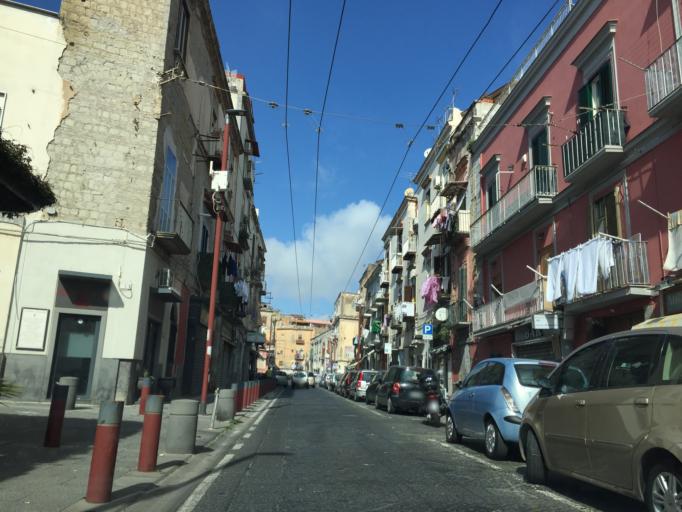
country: IT
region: Campania
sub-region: Provincia di Napoli
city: Portici
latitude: 40.8070
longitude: 14.3488
